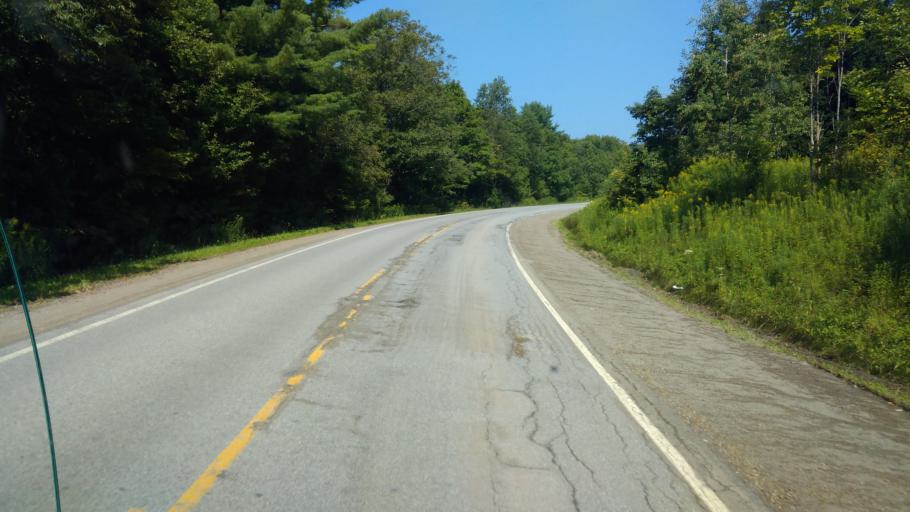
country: US
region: New York
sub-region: Allegany County
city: Bolivar
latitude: 42.0945
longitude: -78.1720
